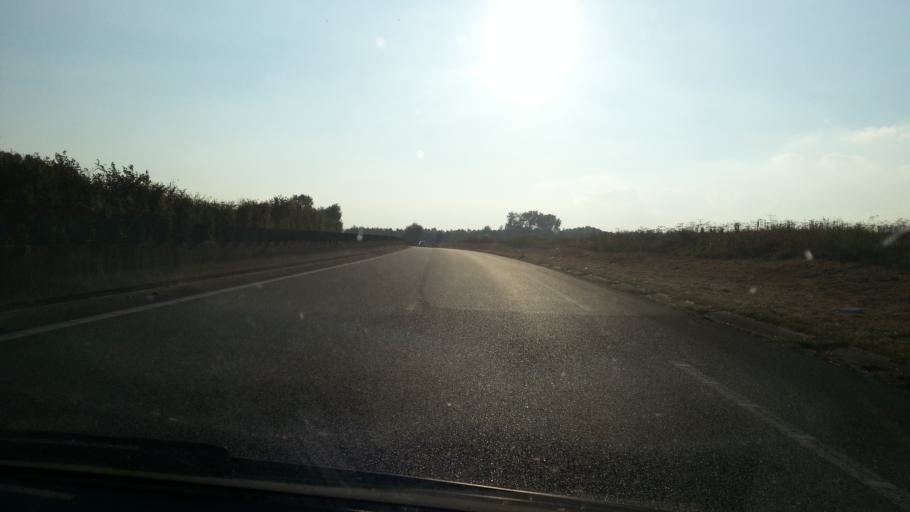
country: FR
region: Picardie
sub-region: Departement de l'Oise
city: Coudun
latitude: 49.4730
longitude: 2.8341
